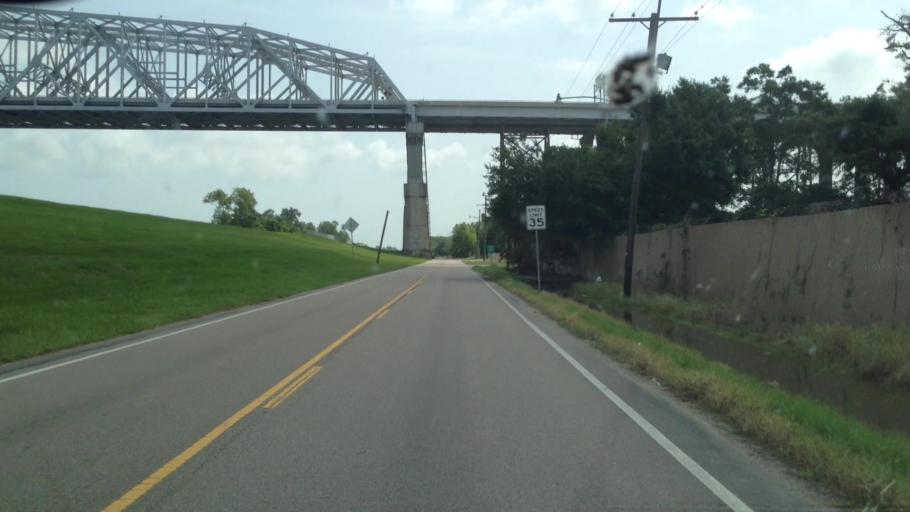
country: US
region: Louisiana
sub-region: Jefferson Parish
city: Bridge City
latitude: 29.9394
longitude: -90.1679
